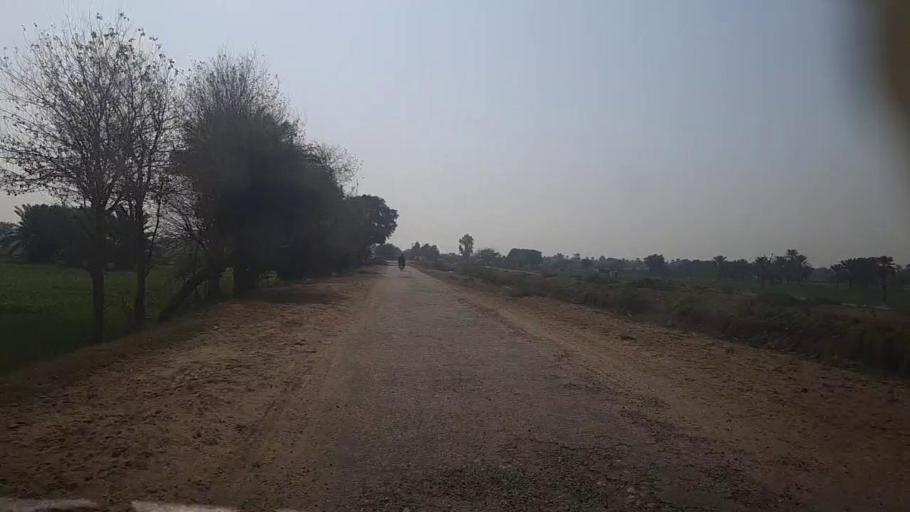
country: PK
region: Sindh
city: Kot Diji
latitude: 27.3679
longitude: 68.7488
